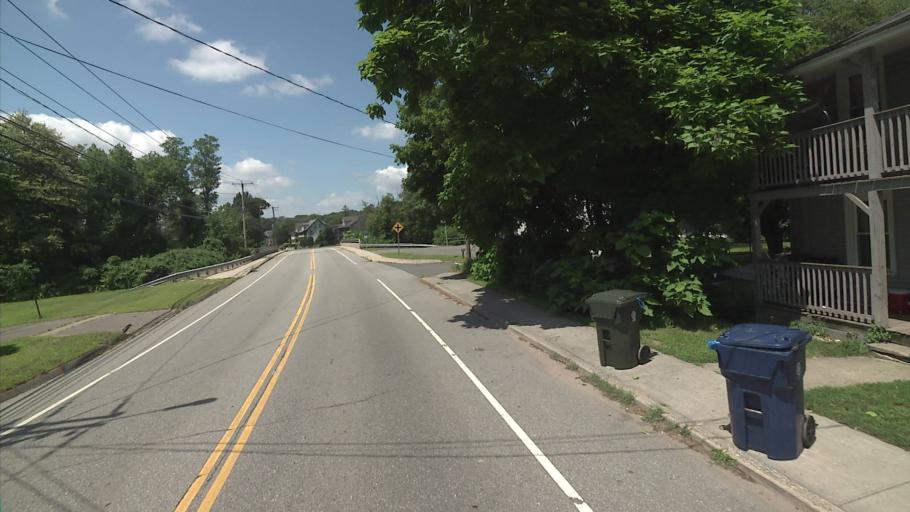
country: US
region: Connecticut
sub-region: Windham County
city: Willimantic
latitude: 41.7159
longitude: -72.1932
